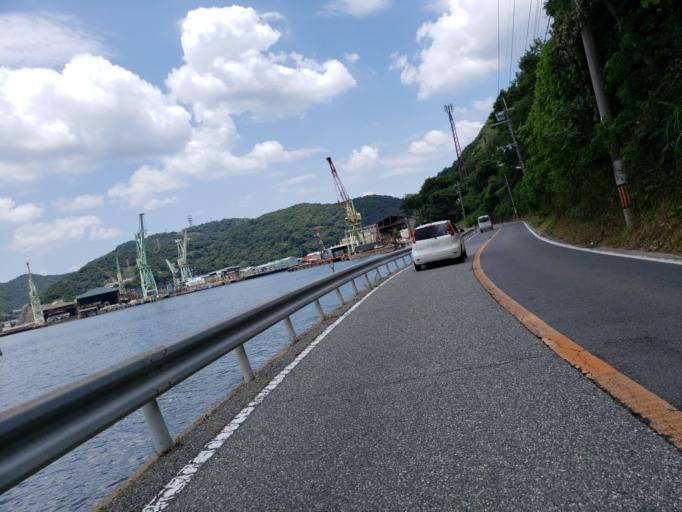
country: JP
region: Hyogo
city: Aioi
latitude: 34.7887
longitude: 134.4725
